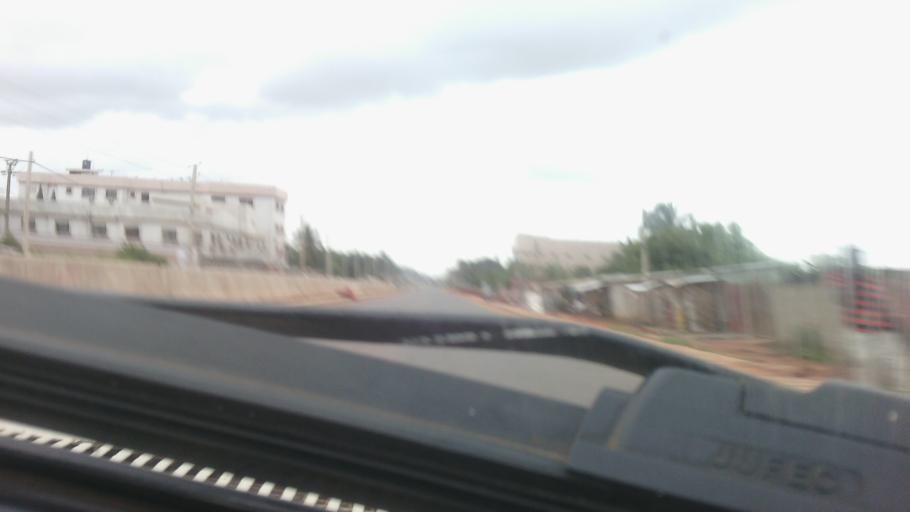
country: BJ
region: Atlantique
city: Ouidah
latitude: 6.3692
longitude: 2.0672
